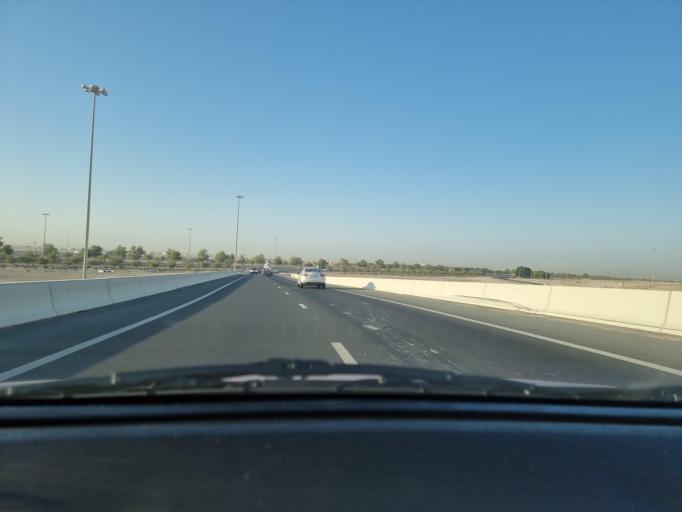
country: AE
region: Abu Dhabi
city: Abu Dhabi
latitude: 24.4165
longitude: 54.7122
